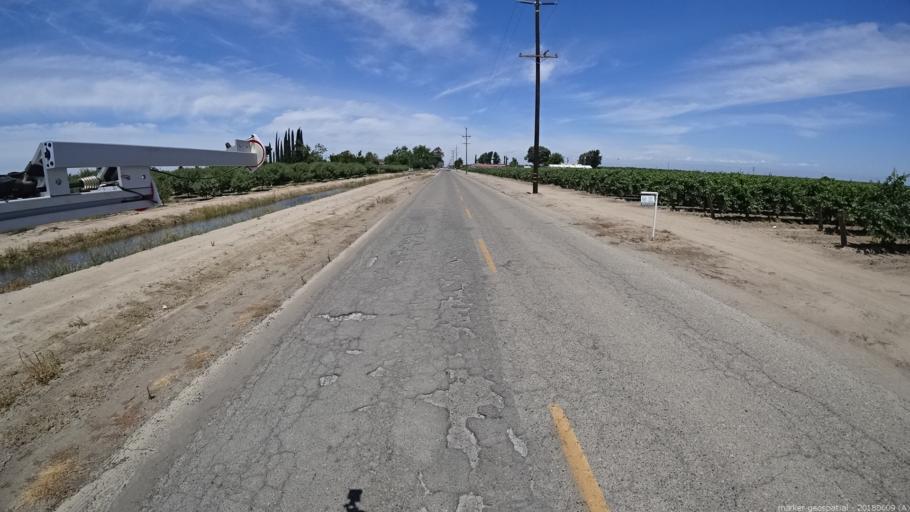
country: US
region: California
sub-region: Madera County
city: Parkwood
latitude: 36.8774
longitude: -120.1104
